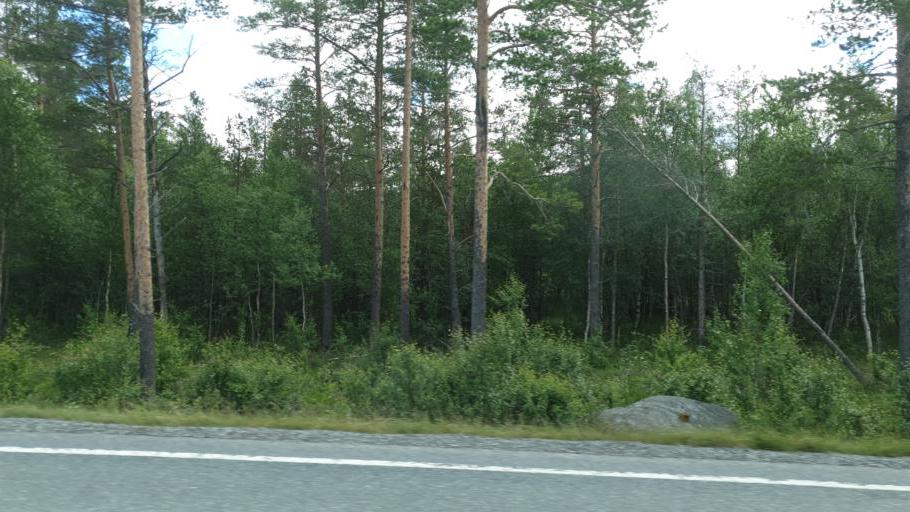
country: NO
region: Sor-Trondelag
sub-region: Oppdal
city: Oppdal
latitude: 62.6515
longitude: 9.8612
